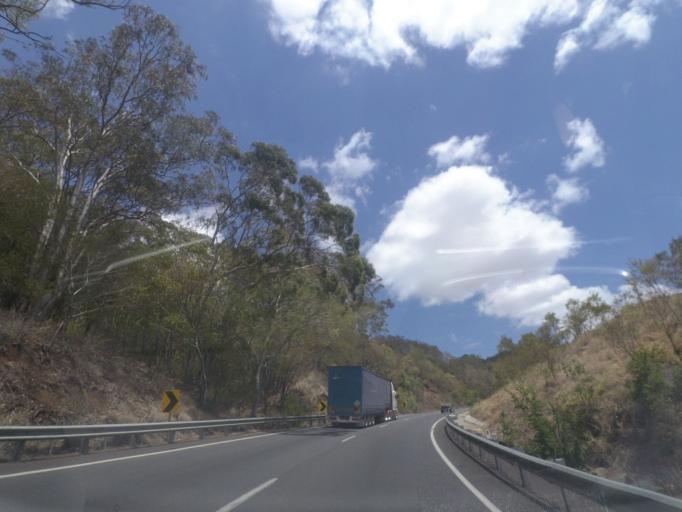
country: AU
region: Queensland
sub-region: Toowoomba
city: East Toowoomba
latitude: -27.5729
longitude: 151.9841
